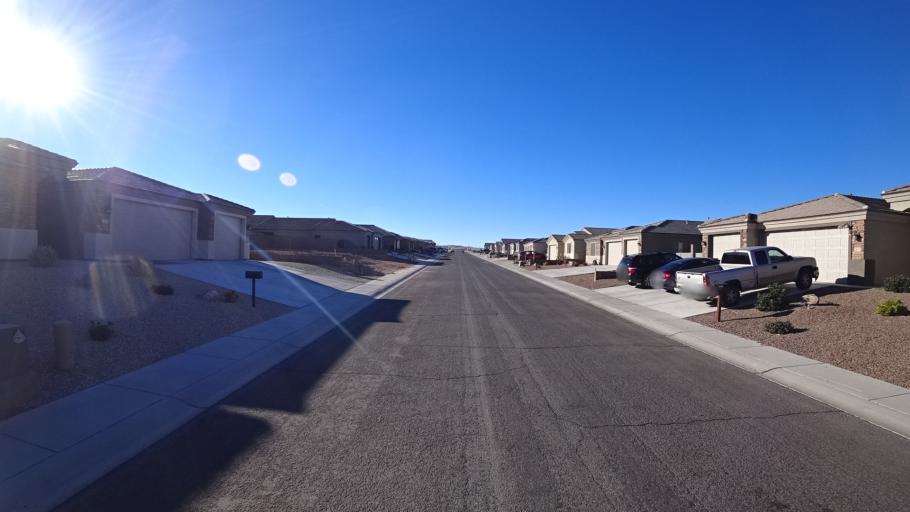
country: US
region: Arizona
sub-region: Mohave County
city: Kingman
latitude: 35.1907
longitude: -114.0058
